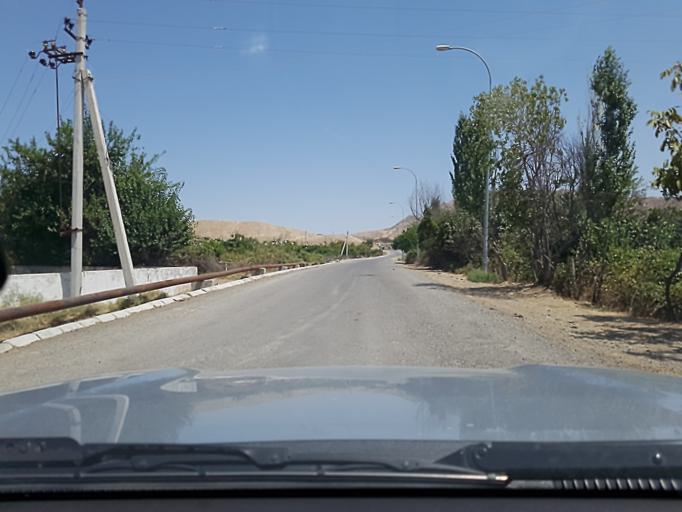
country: TM
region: Balkan
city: Magtymguly
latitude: 38.4381
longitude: 56.4843
